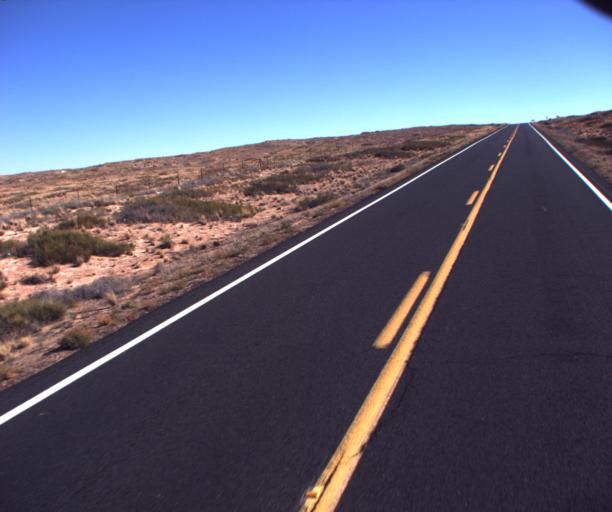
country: US
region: Arizona
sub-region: Coconino County
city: Tuba City
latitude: 36.0202
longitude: -111.1249
